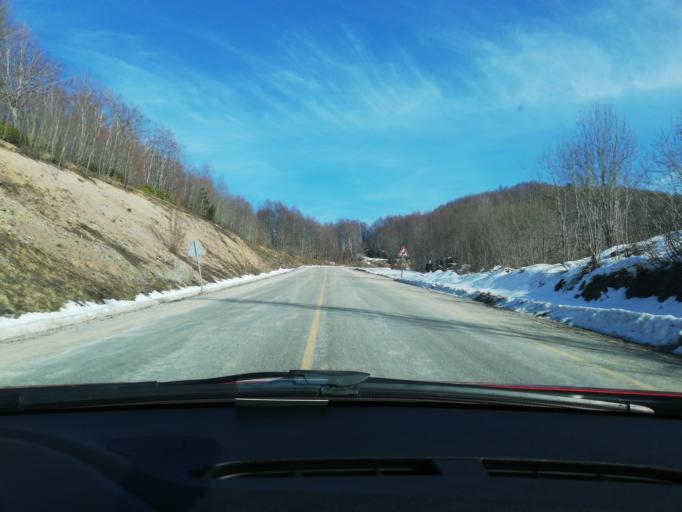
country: TR
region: Kastamonu
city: Cide
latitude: 41.8532
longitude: 33.0653
